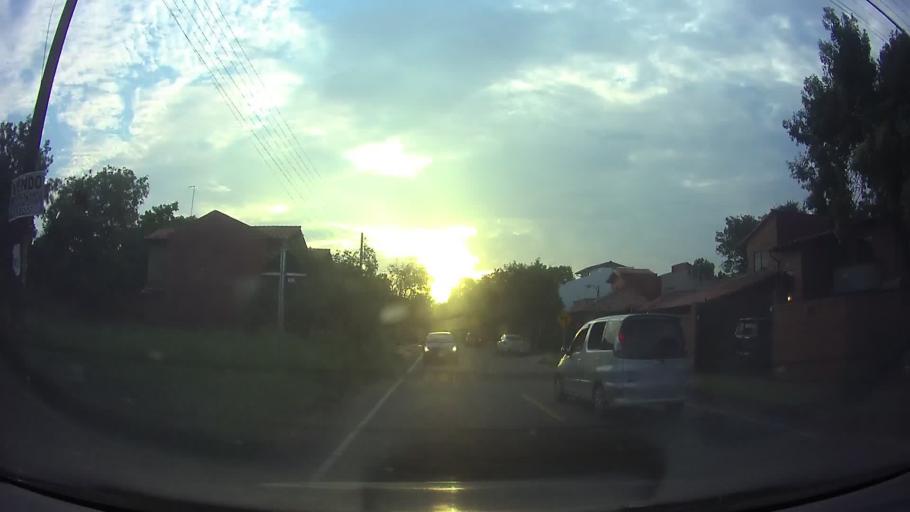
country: PY
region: Central
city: San Lorenzo
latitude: -25.2552
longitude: -57.5028
